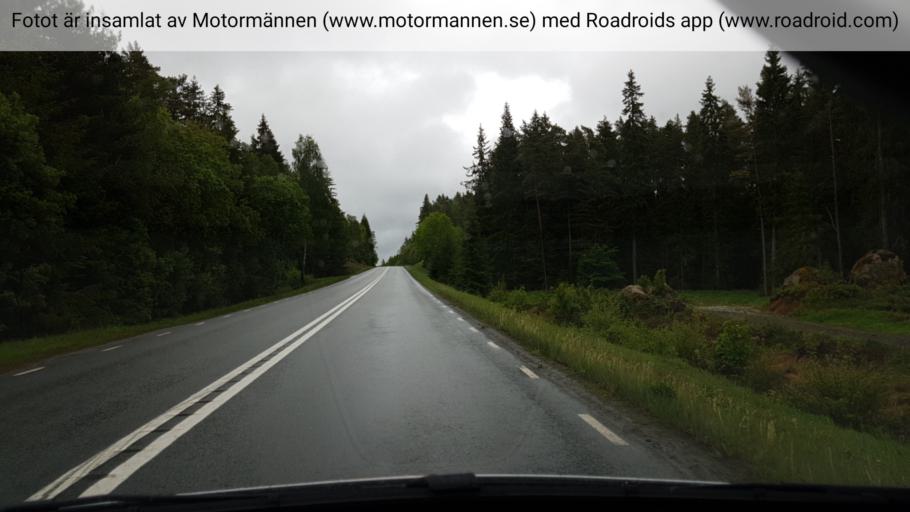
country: SE
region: Joenkoeping
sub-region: Jonkopings Kommun
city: Tenhult
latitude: 57.7731
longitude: 14.4799
